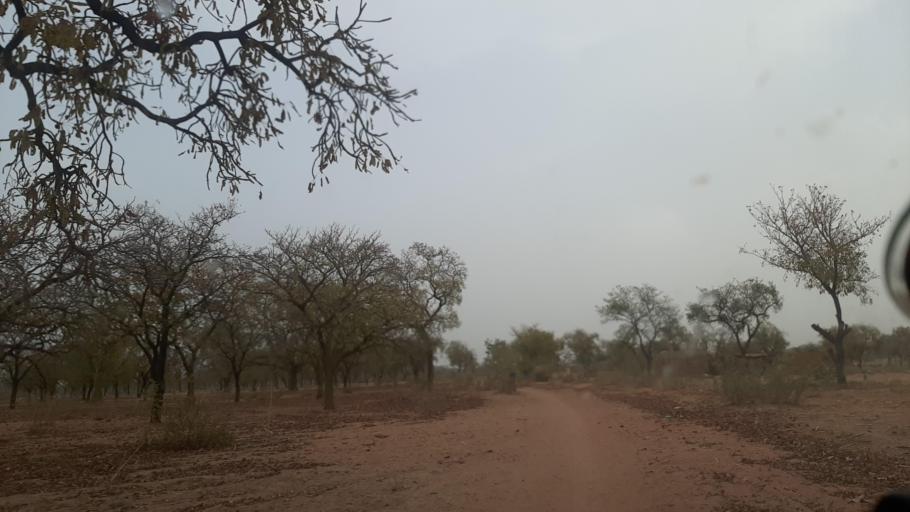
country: BF
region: Boucle du Mouhoun
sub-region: Province des Banwa
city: Salanso
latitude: 11.8677
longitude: -4.4452
